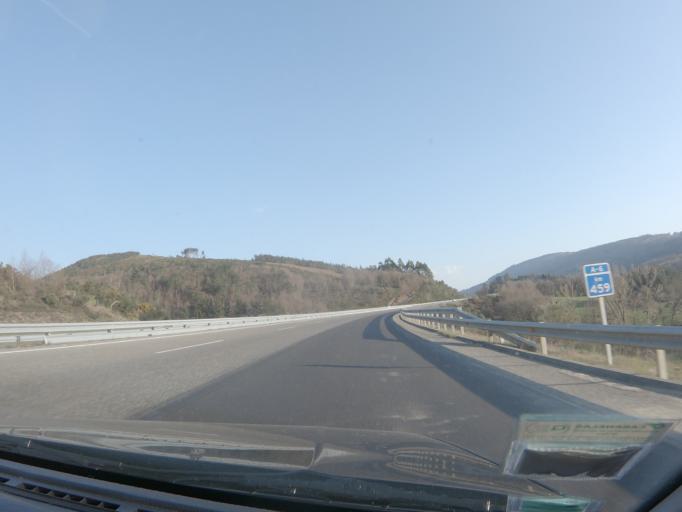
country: ES
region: Galicia
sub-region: Provincia de Lugo
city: Becerrea
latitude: 42.9085
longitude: -7.1921
